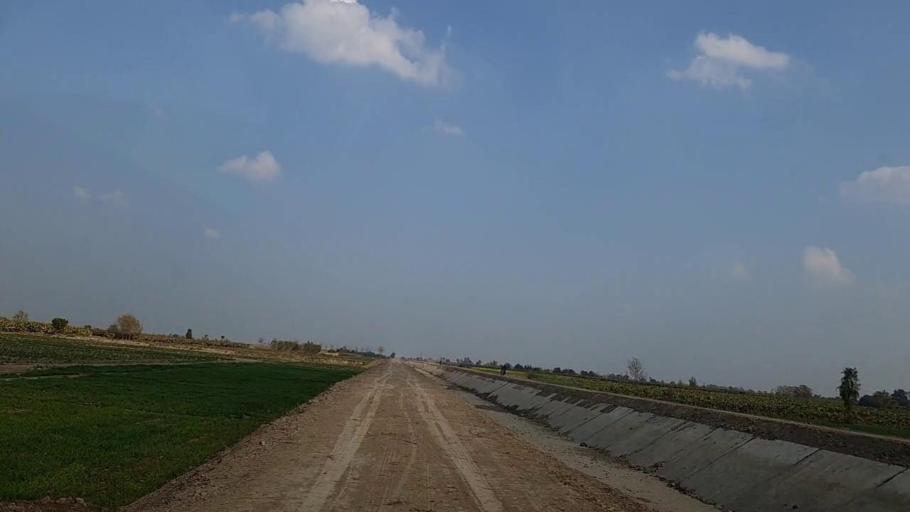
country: PK
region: Sindh
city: Sakrand
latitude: 26.1476
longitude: 68.3647
